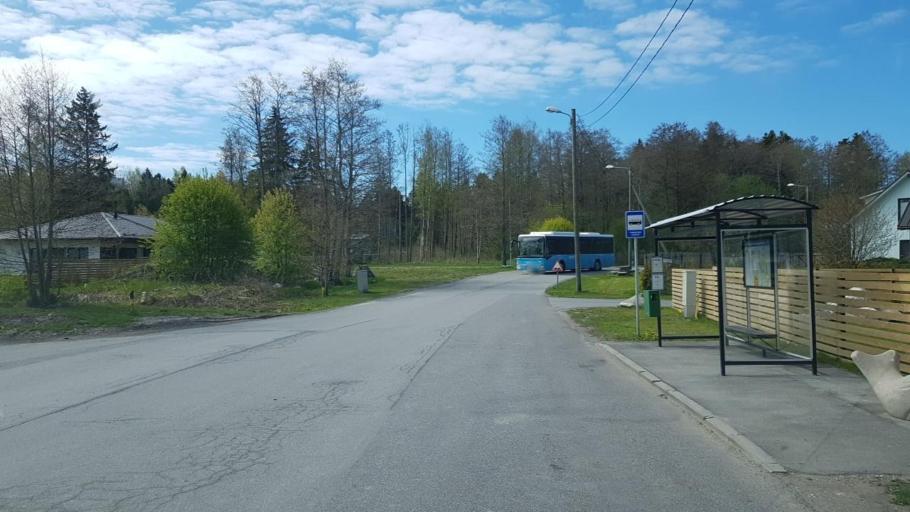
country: EE
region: Harju
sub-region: Viimsi vald
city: Viimsi
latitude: 59.5299
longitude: 24.8858
